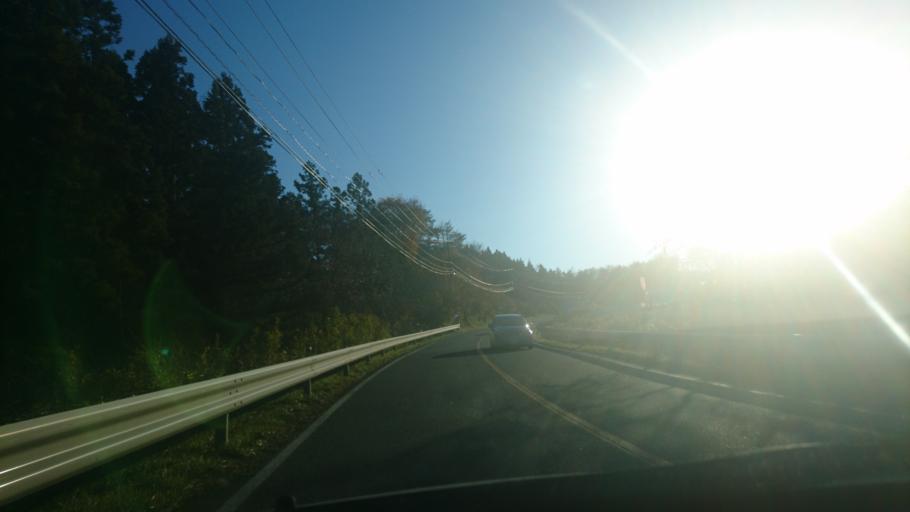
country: JP
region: Iwate
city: Ichinoseki
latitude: 38.9031
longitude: 141.2180
